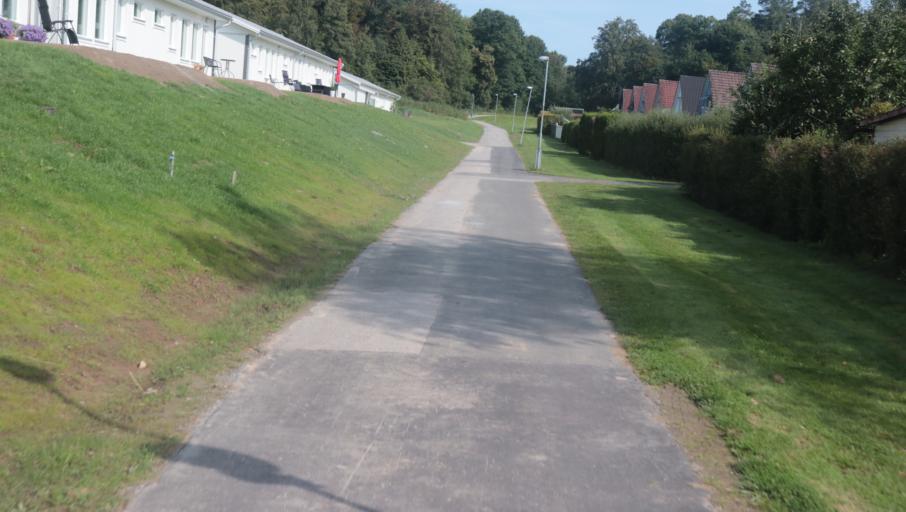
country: SE
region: Blekinge
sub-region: Karlshamns Kommun
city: Karlshamn
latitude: 56.1986
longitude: 14.8454
